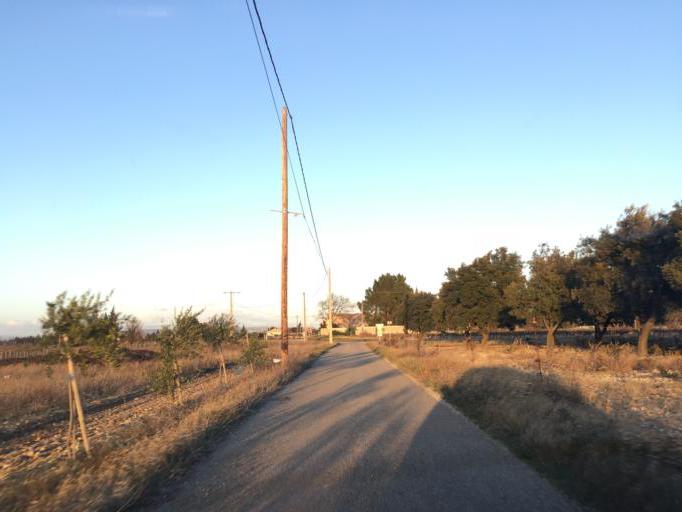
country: FR
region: Provence-Alpes-Cote d'Azur
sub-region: Departement du Vaucluse
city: Camaret-sur-Aigues
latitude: 44.1466
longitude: 4.8865
